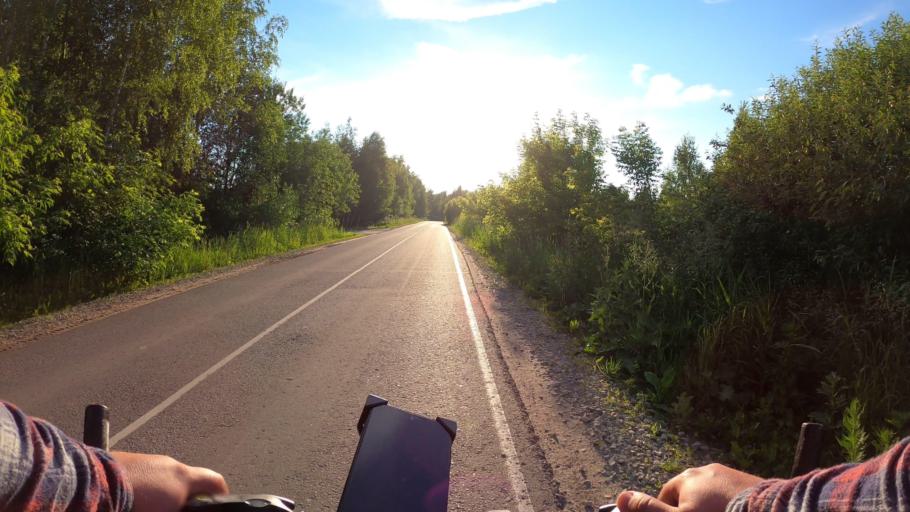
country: RU
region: Moskovskaya
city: Ashitkovo
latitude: 55.4272
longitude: 38.5701
